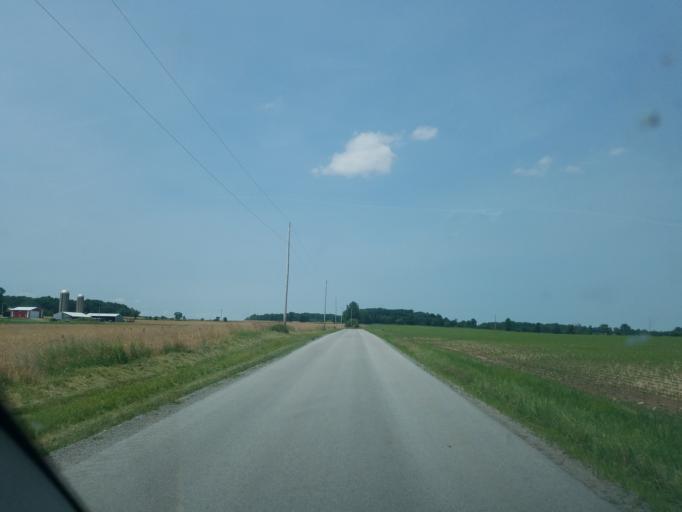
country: US
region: Ohio
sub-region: Wyandot County
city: Carey
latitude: 41.0301
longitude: -83.4488
